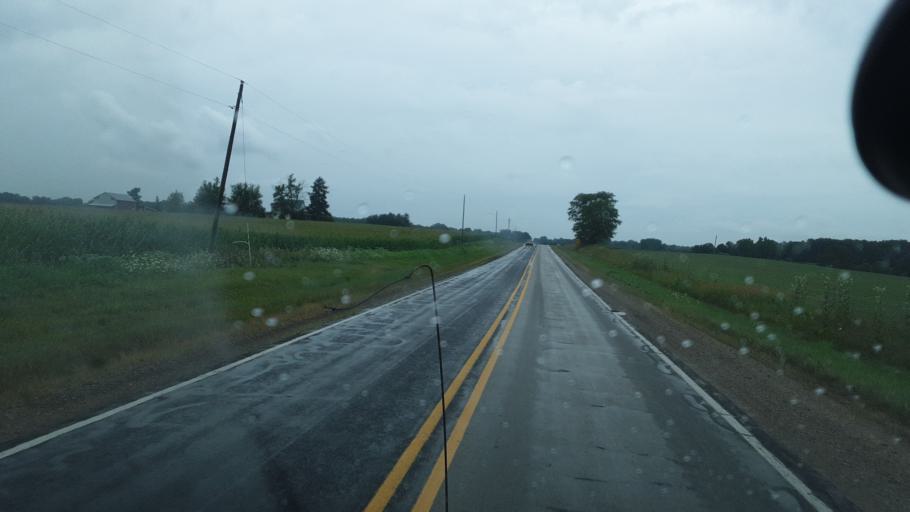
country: US
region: Indiana
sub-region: Steuben County
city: Hamilton
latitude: 41.5592
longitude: -84.8133
